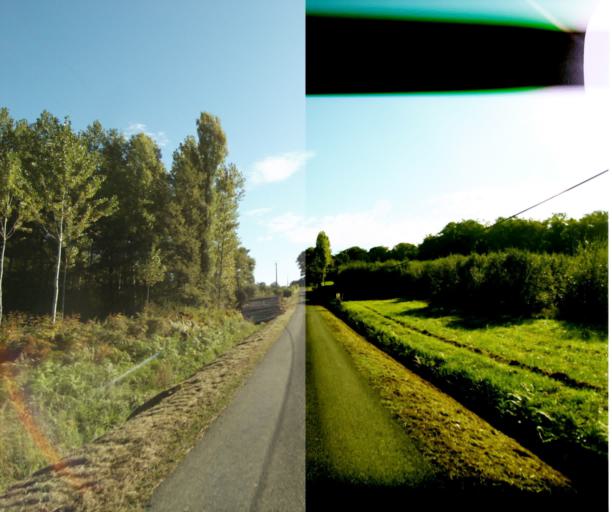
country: FR
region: Midi-Pyrenees
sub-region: Departement du Gers
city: Cazaubon
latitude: 43.9100
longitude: -0.0098
